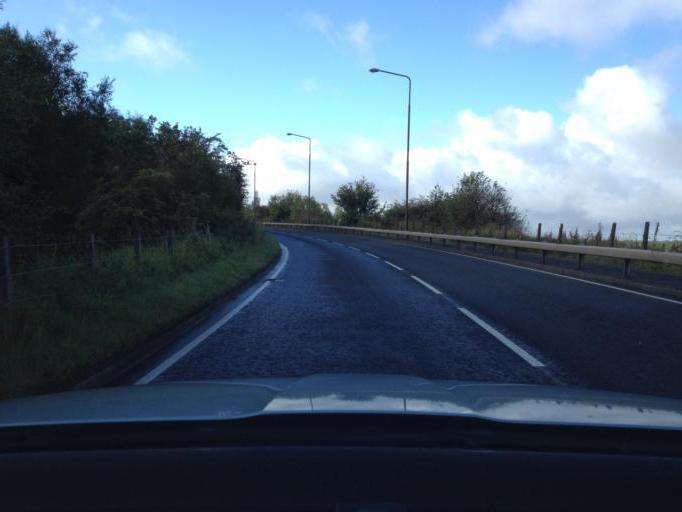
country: GB
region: Scotland
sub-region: West Lothian
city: West Calder
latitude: 55.8555
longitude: -3.5645
